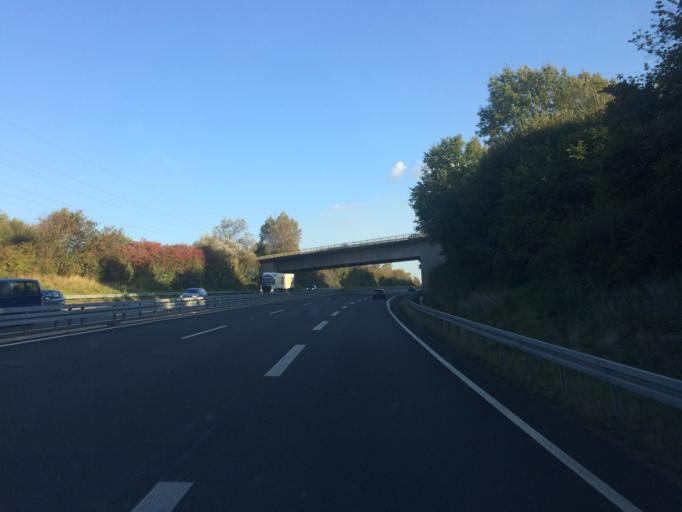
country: DE
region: Saarland
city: Illingen
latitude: 49.3604
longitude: 7.0155
